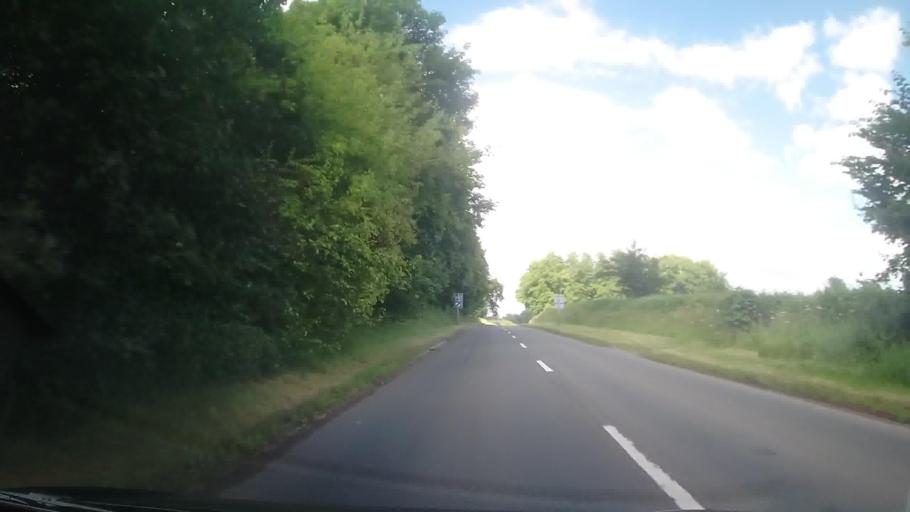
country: GB
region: England
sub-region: Shropshire
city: Whittington
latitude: 52.8782
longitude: -2.9968
